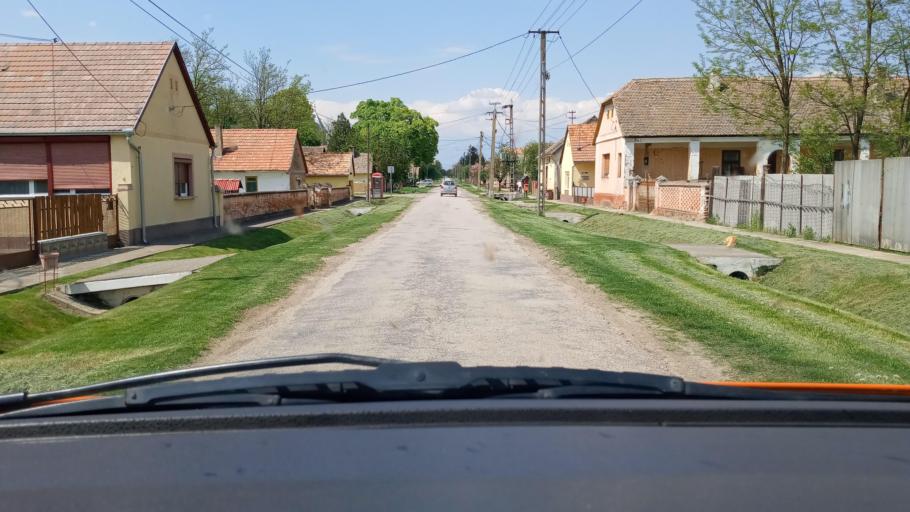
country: HR
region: Osjecko-Baranjska
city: Beli Manastir
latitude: 45.7996
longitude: 18.5238
